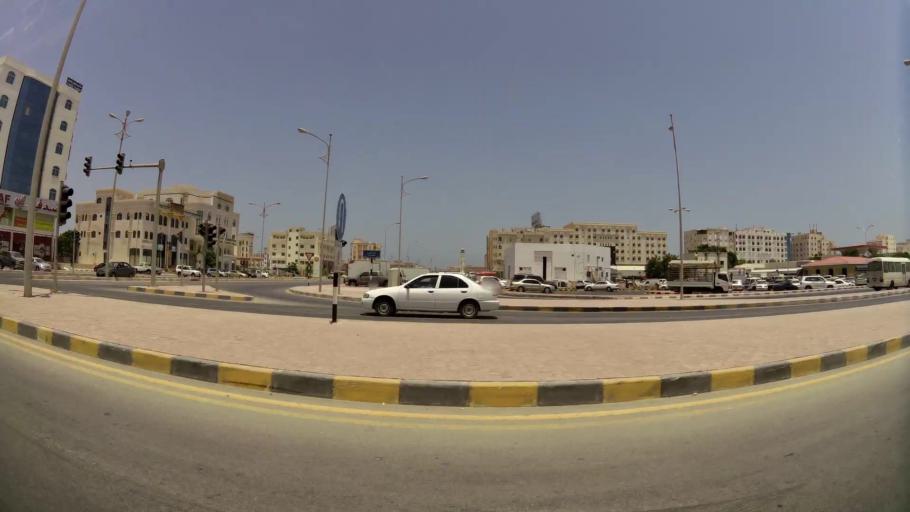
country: OM
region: Zufar
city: Salalah
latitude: 17.0199
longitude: 54.1002
